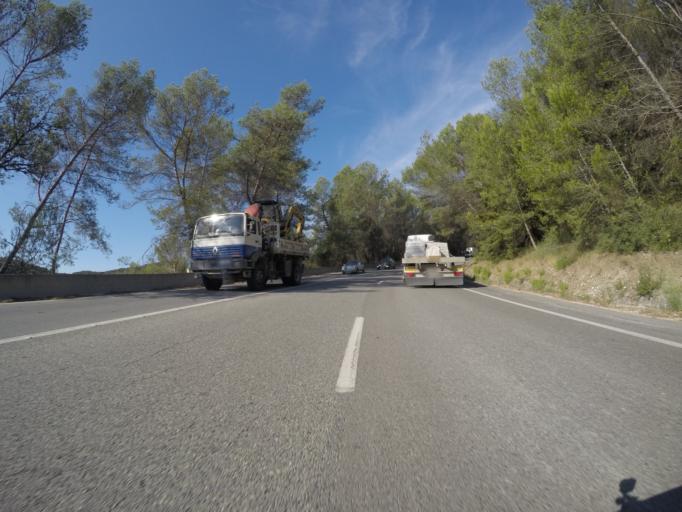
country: FR
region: Provence-Alpes-Cote d'Azur
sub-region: Departement des Alpes-Maritimes
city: Biot
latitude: 43.6564
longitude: 7.0895
